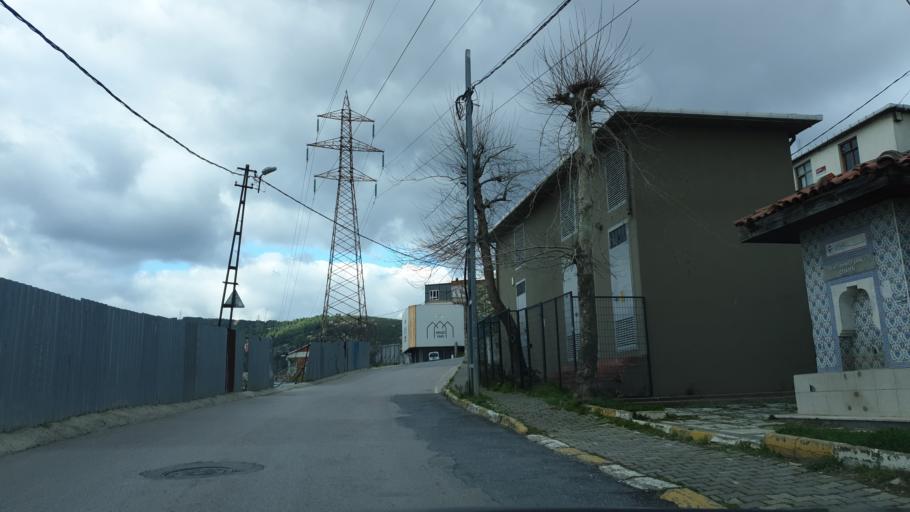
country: TR
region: Istanbul
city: Pendik
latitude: 40.8978
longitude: 29.2369
